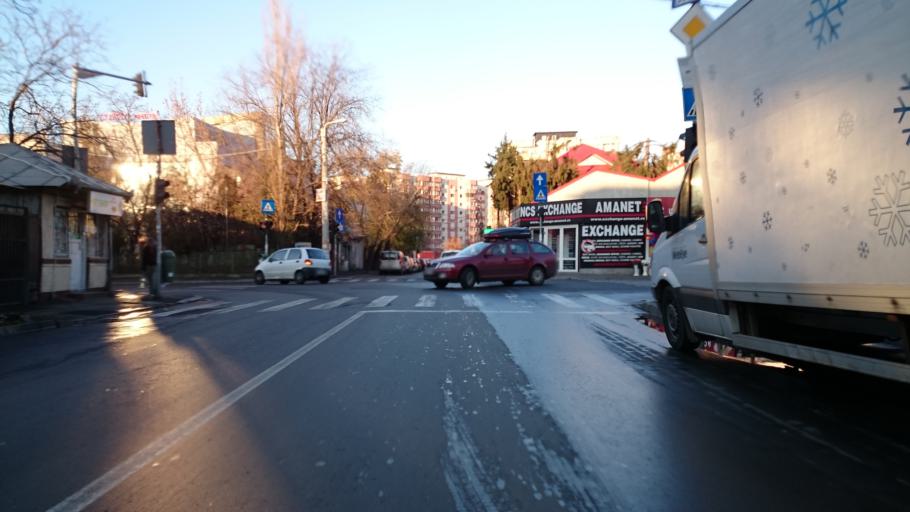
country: RO
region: Bucuresti
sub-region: Municipiul Bucuresti
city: Bucuresti
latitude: 44.4146
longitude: 26.0617
